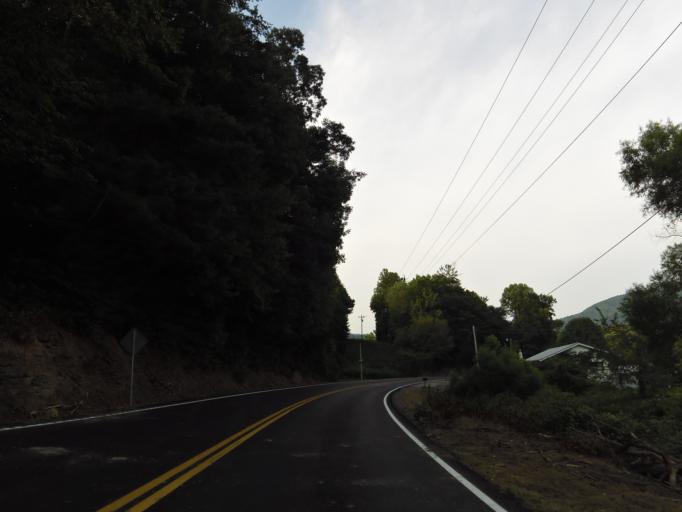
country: US
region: Tennessee
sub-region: Morgan County
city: Coalfield
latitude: 36.0828
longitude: -84.4574
